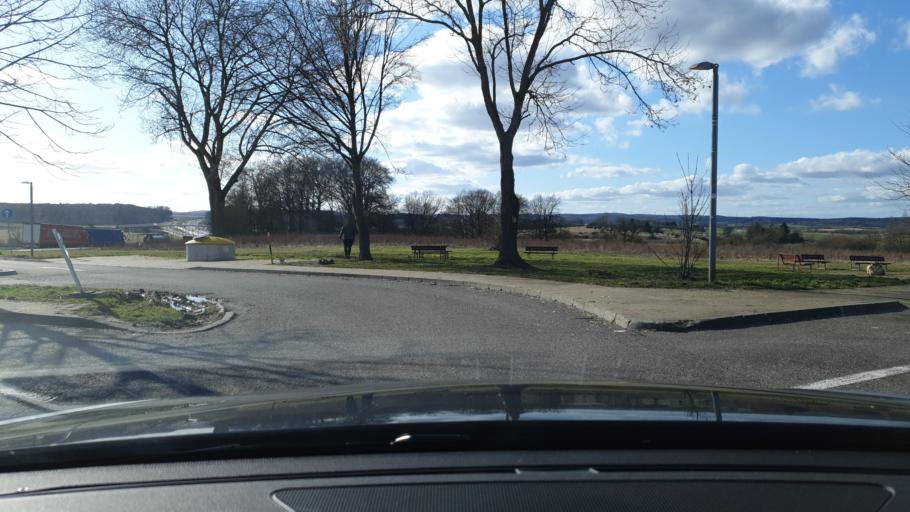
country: DE
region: Baden-Wuerttemberg
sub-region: Tuebingen Region
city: Nellingen
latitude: 48.5208
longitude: 9.8059
